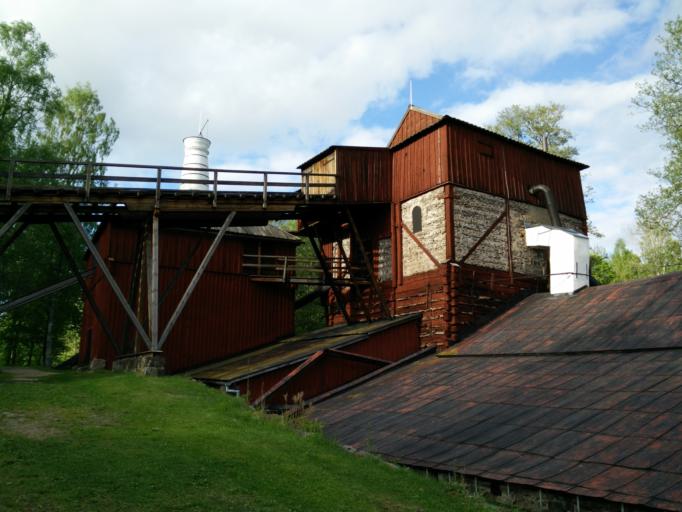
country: SE
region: Vaestmanland
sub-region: Norbergs Kommun
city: Norberg
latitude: 59.9673
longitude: 16.0103
